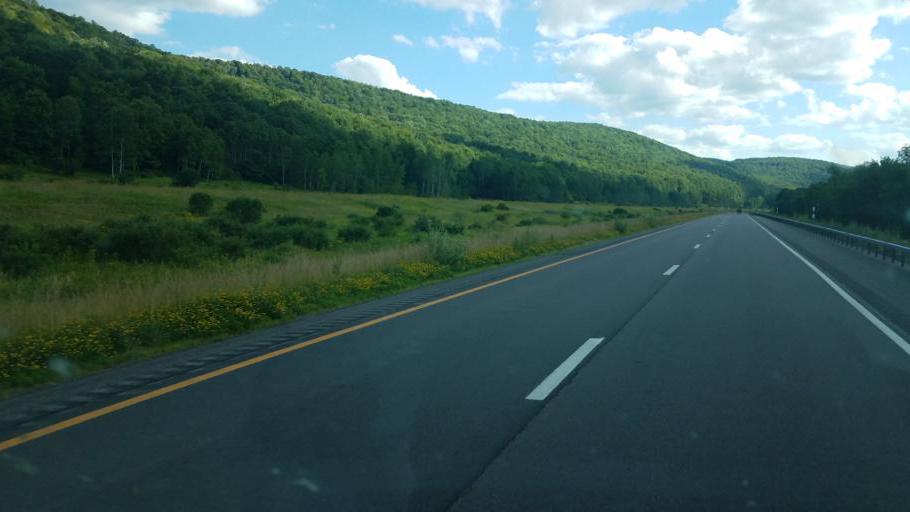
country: US
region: New York
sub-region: Allegany County
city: Cuba
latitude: 42.2016
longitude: -78.3304
